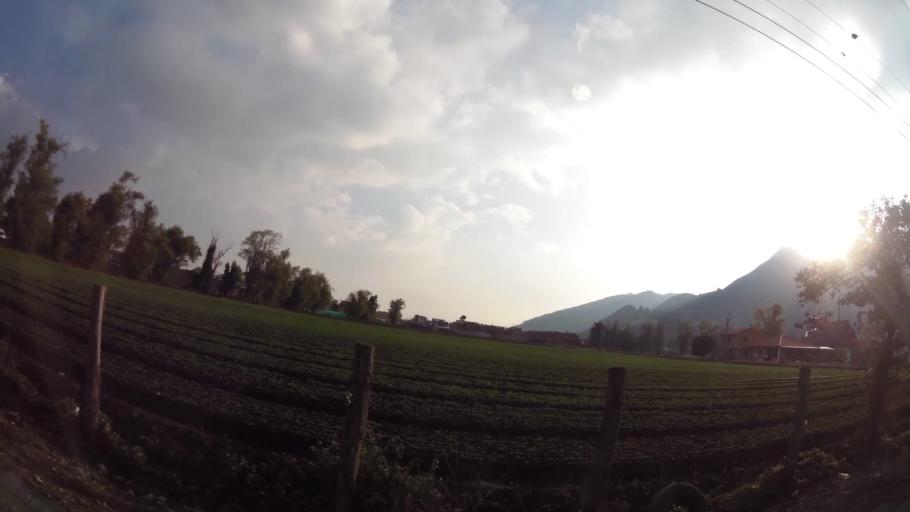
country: CO
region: Cundinamarca
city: Cota
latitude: 4.8170
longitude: -74.0987
